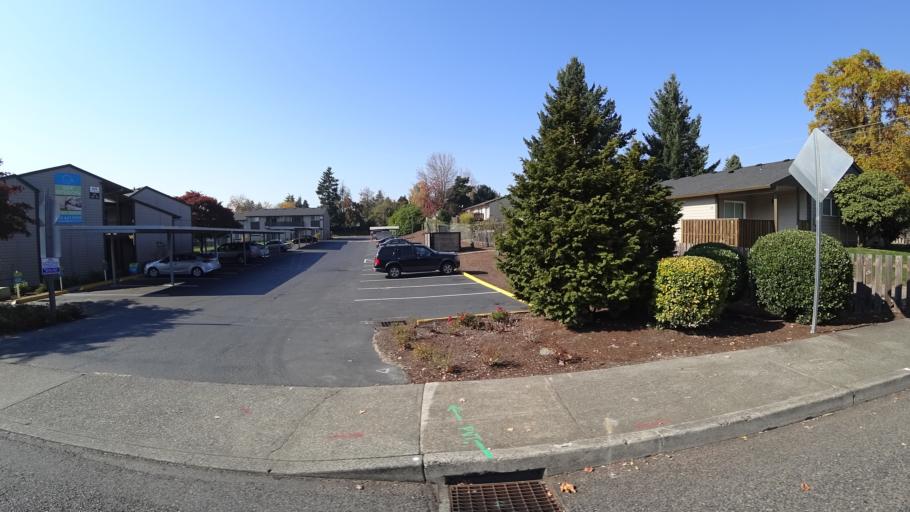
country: US
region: Oregon
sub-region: Multnomah County
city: Gresham
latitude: 45.4967
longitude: -122.4384
